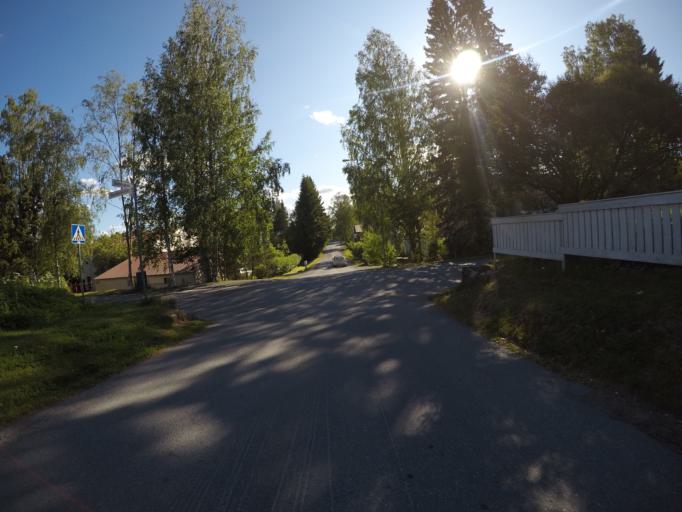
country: FI
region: Haeme
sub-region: Haemeenlinna
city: Haemeenlinna
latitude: 61.0081
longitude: 24.4858
